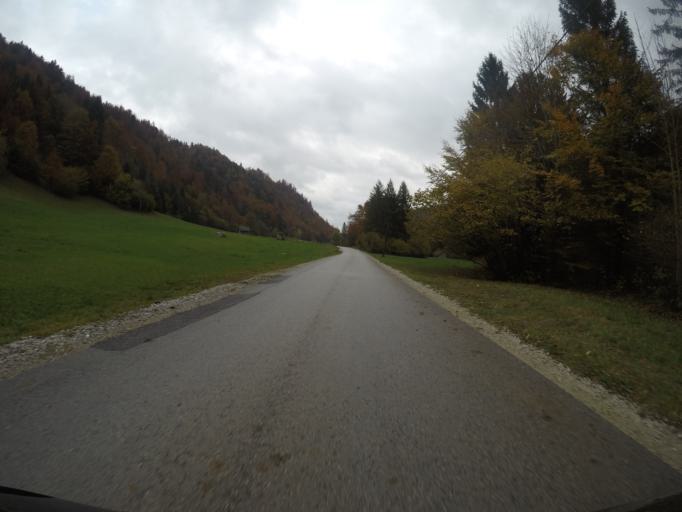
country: SI
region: Gorje
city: Zgornje Gorje
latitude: 46.3922
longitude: 14.0206
